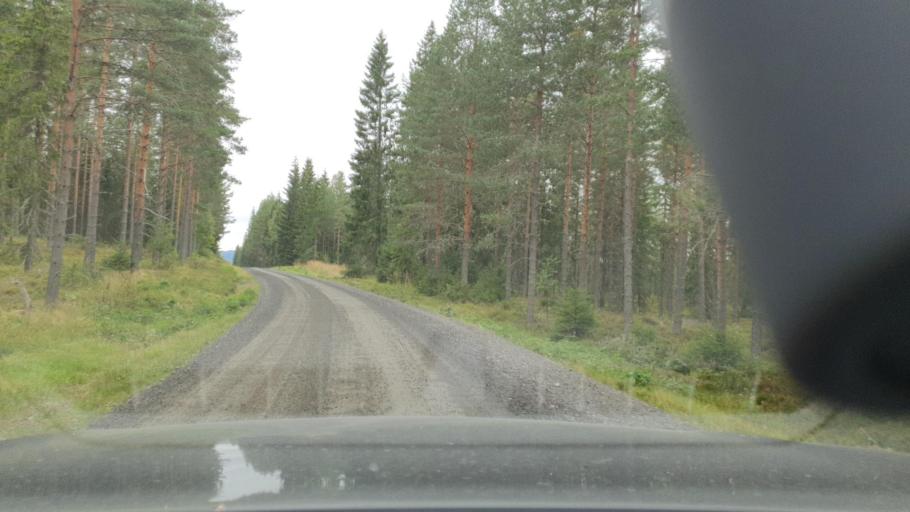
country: SE
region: Vaermland
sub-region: Torsby Kommun
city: Torsby
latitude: 60.3425
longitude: 12.8044
